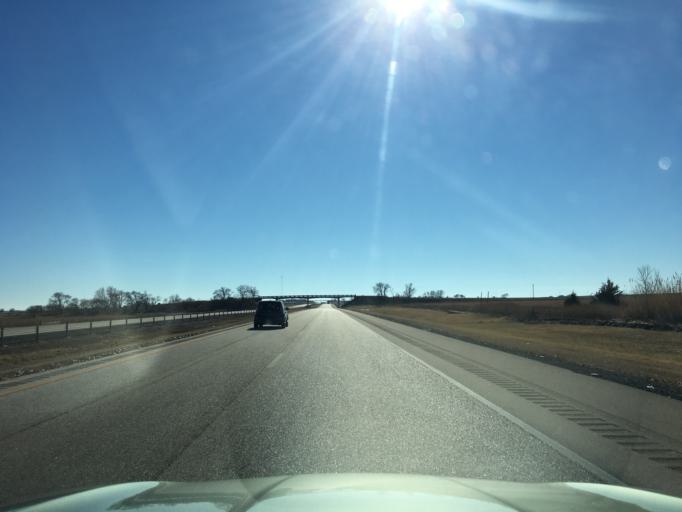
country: US
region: Oklahoma
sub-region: Kay County
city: Blackwell
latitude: 36.8869
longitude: -97.3526
